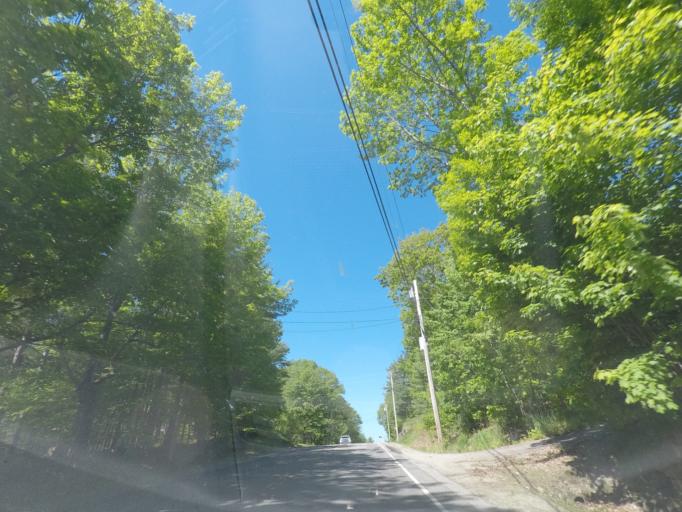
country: US
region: Maine
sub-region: Kennebec County
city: Gardiner
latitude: 44.2296
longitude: -69.8217
